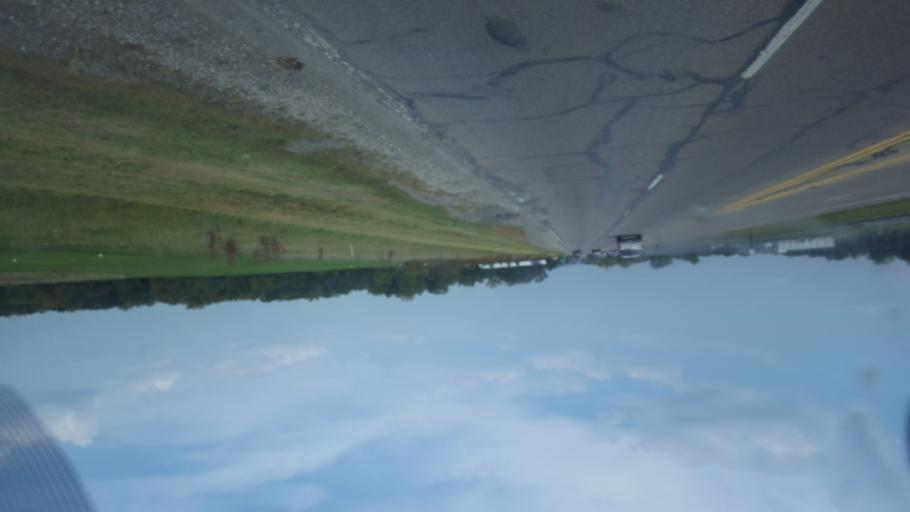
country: US
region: Ohio
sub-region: Franklin County
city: Whitehall
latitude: 39.9913
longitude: -82.8689
